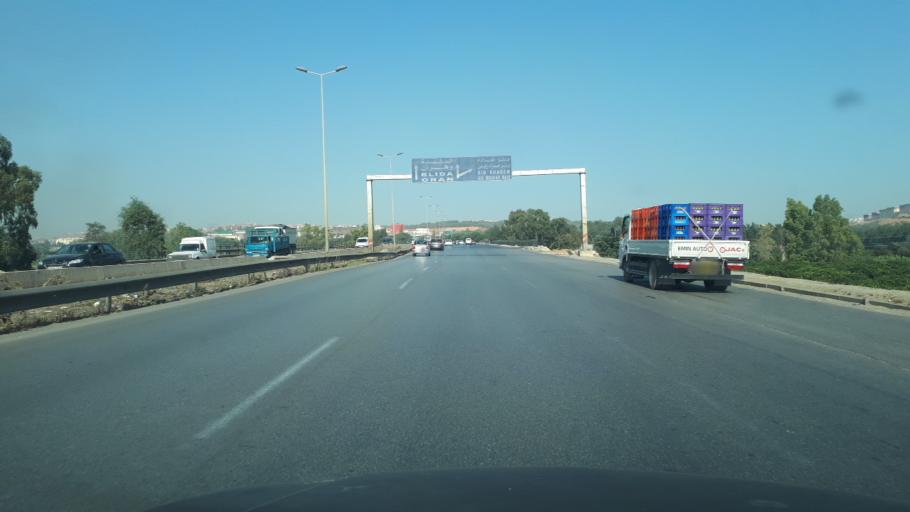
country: DZ
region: Tipaza
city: Baraki
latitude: 36.6776
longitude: 3.0682
